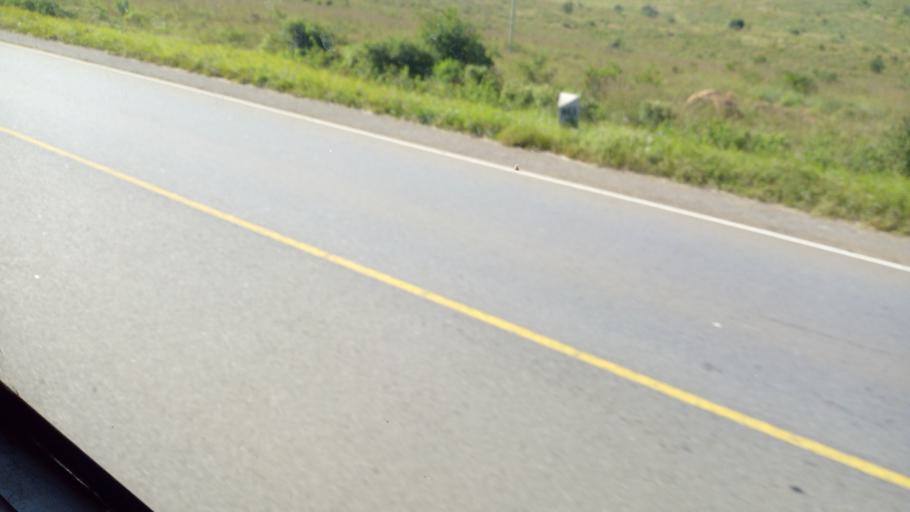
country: UG
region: Central Region
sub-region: Lyantonde District
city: Lyantonde
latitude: -0.4483
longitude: 31.0630
